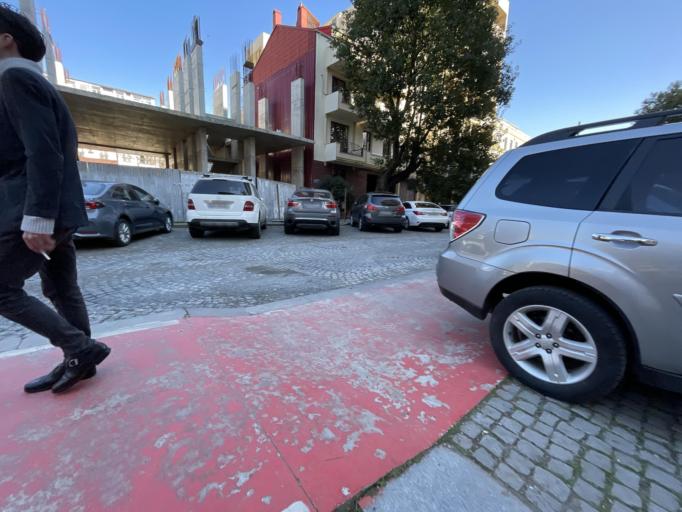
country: GE
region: Ajaria
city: Batumi
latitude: 41.6496
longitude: 41.6323
